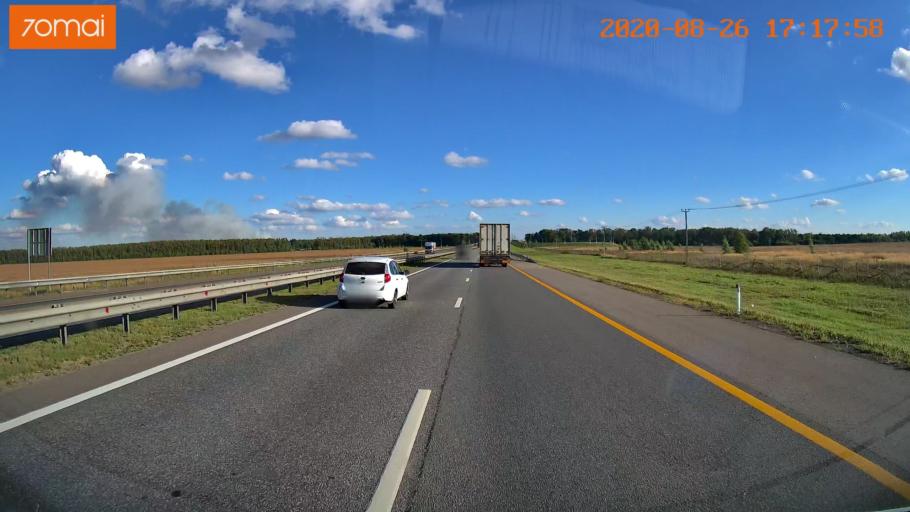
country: RU
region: Tula
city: Volovo
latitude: 53.6163
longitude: 38.0925
